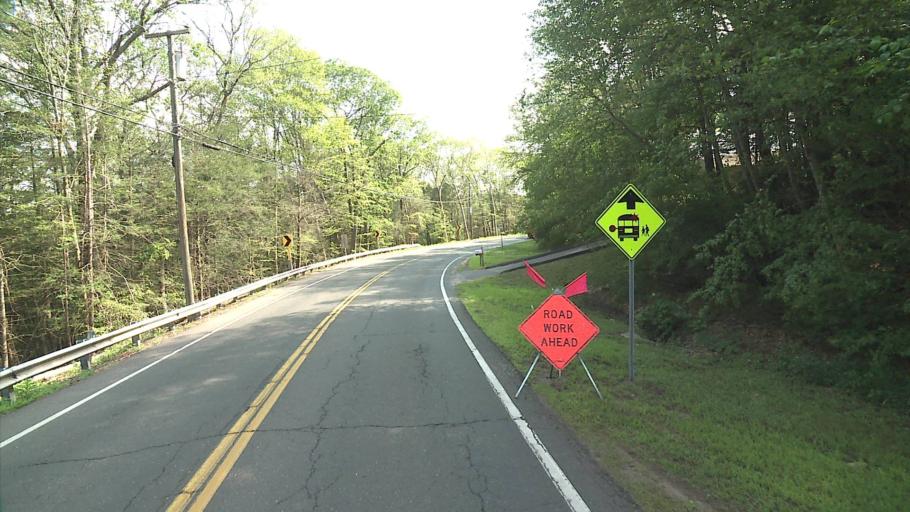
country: US
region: Connecticut
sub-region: Middlesex County
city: Moodus
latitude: 41.4961
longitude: -72.4580
